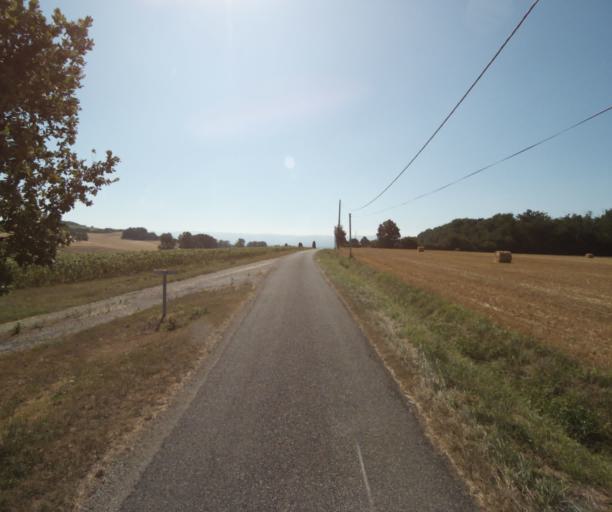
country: FR
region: Midi-Pyrenees
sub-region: Departement de la Haute-Garonne
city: Saint-Felix-Lauragais
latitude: 43.5015
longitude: 1.9224
